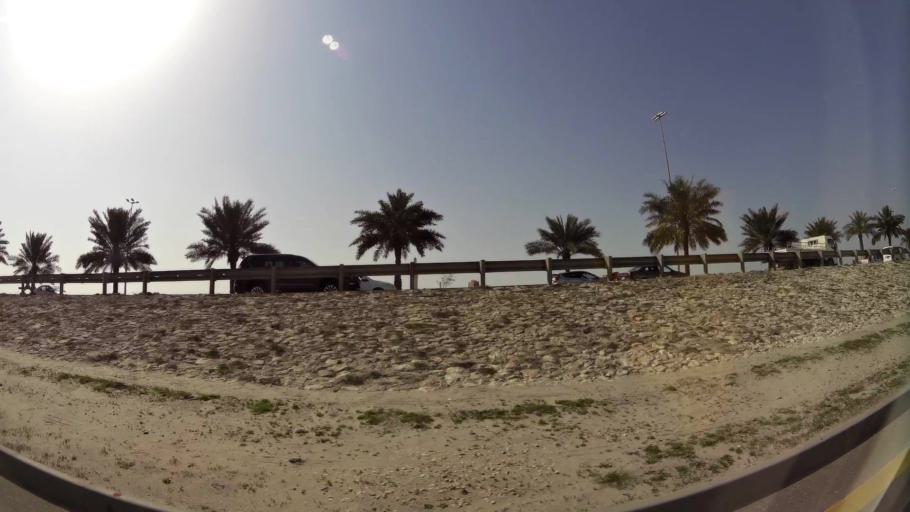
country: BH
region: Manama
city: Jidd Hafs
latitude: 26.2151
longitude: 50.5207
